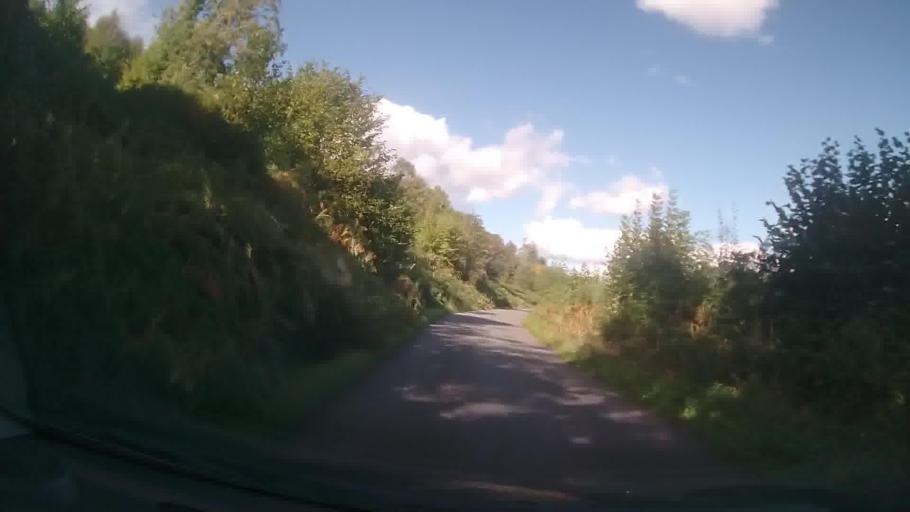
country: GB
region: Wales
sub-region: Caerphilly County Borough
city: Rhymney
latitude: 51.8619
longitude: -3.3121
